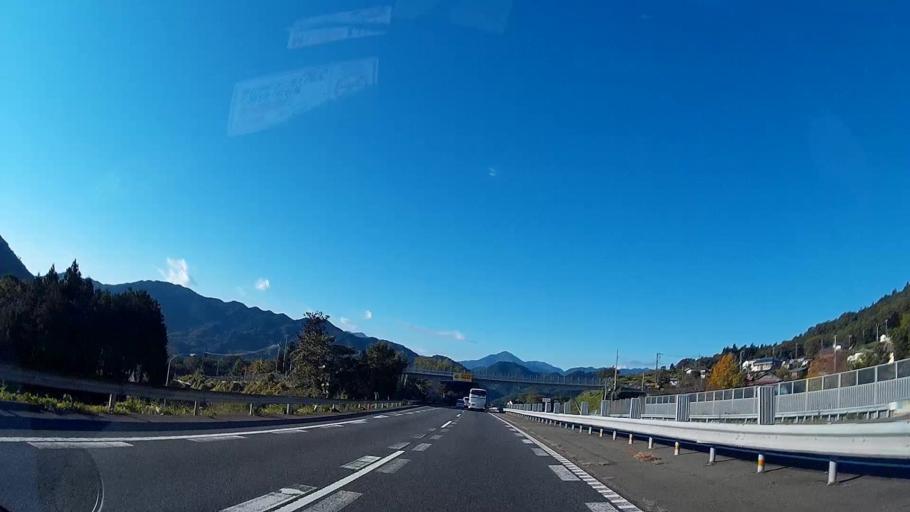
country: JP
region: Yamanashi
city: Uenohara
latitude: 35.6208
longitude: 139.1944
